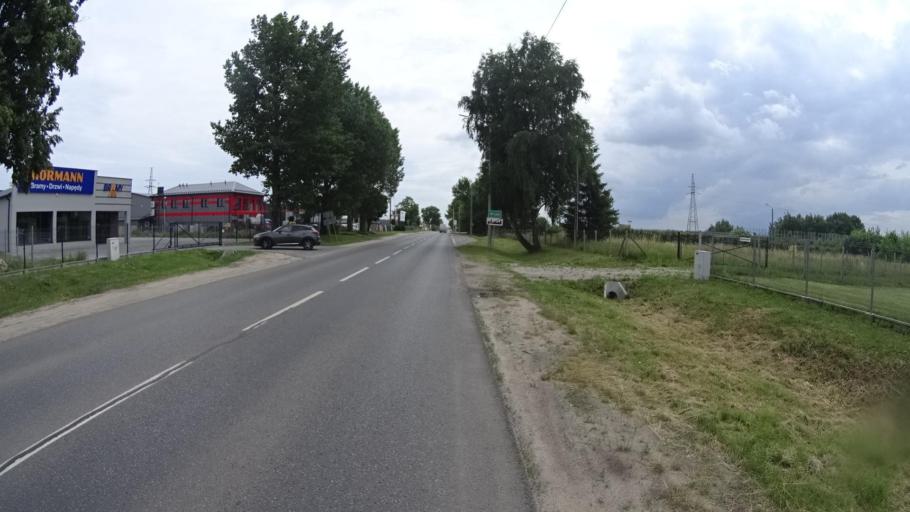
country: PL
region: Masovian Voivodeship
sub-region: Powiat grojecki
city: Grojec
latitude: 51.8512
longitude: 20.8715
